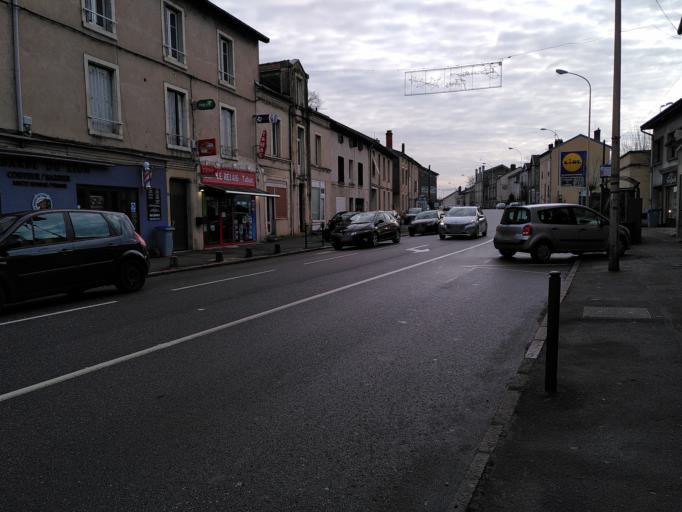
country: FR
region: Lorraine
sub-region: Departement de Meurthe-et-Moselle
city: Frouard
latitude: 48.7596
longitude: 6.1336
